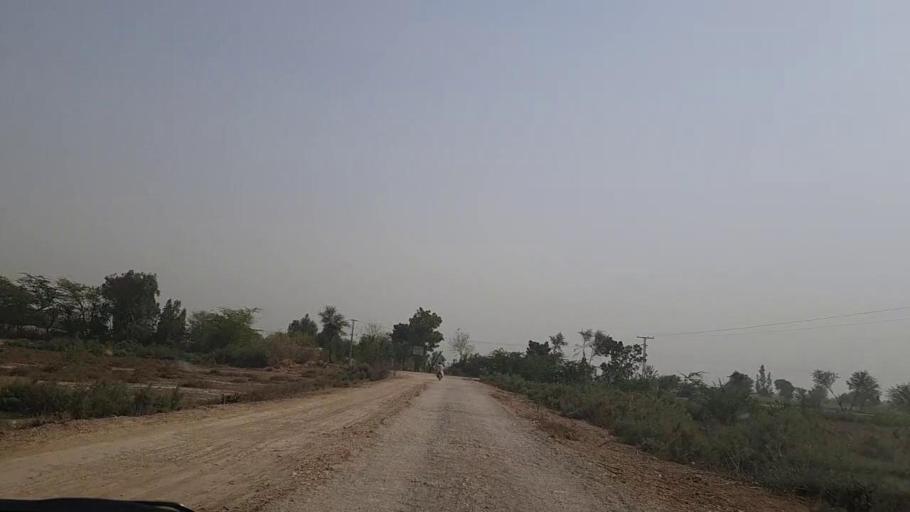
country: PK
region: Sindh
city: Pithoro
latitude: 25.4772
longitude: 69.2223
